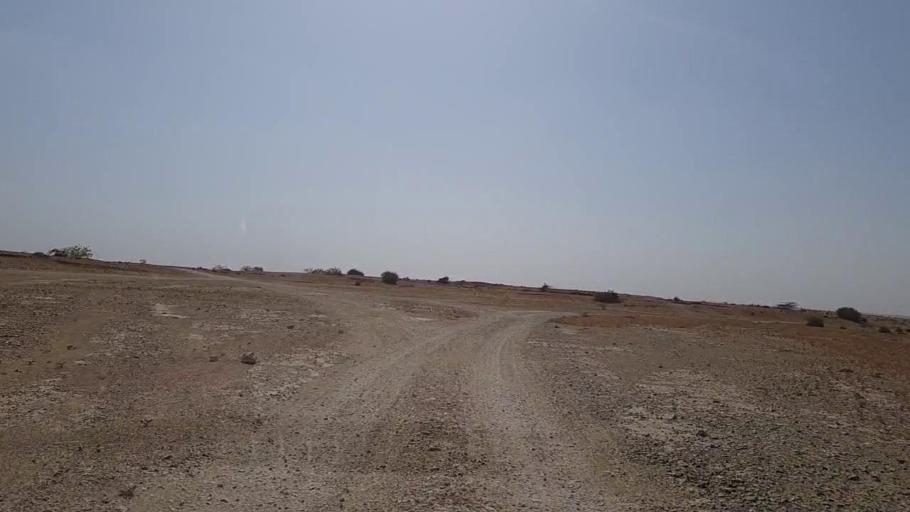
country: PK
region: Sindh
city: Kotri
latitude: 25.1651
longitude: 68.1835
